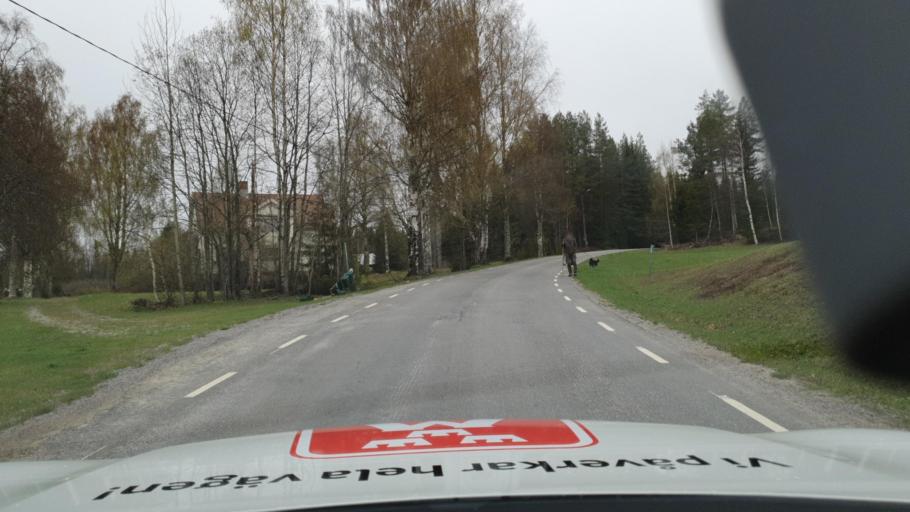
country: SE
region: Vaesterbotten
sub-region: Nordmalings Kommun
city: Nordmaling
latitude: 63.7310
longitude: 19.5033
